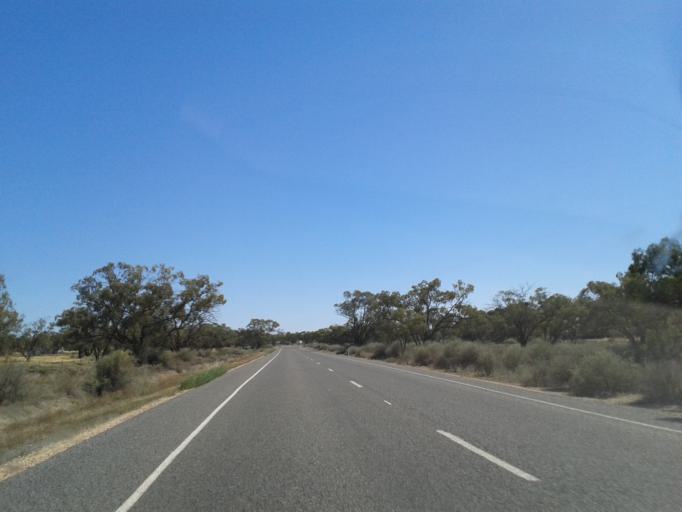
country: AU
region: New South Wales
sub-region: Wentworth
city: Dareton
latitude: -34.1223
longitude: 141.9881
